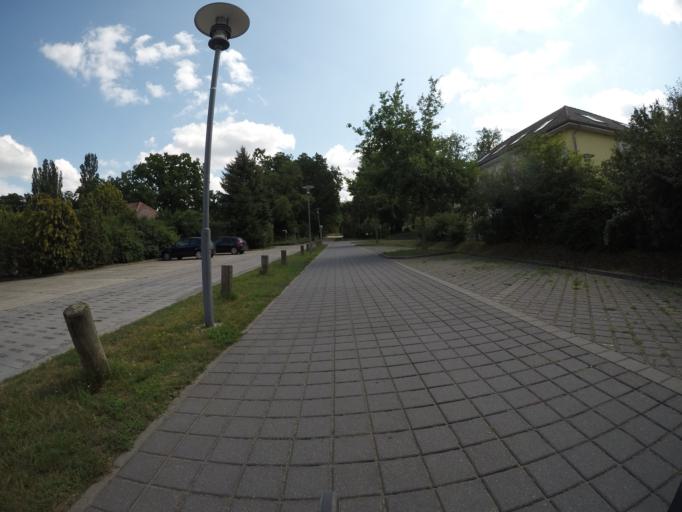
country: DE
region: Brandenburg
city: Werder
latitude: 52.4096
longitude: 12.9771
